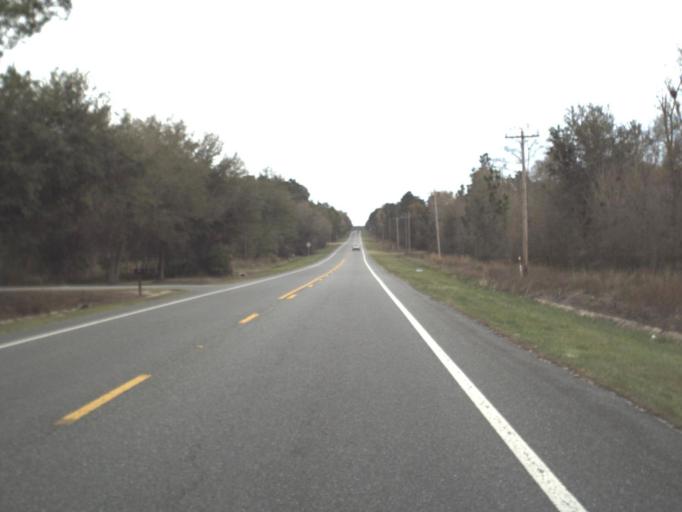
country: US
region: Florida
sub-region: Wakulla County
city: Crawfordville
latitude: 30.2747
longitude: -84.3805
